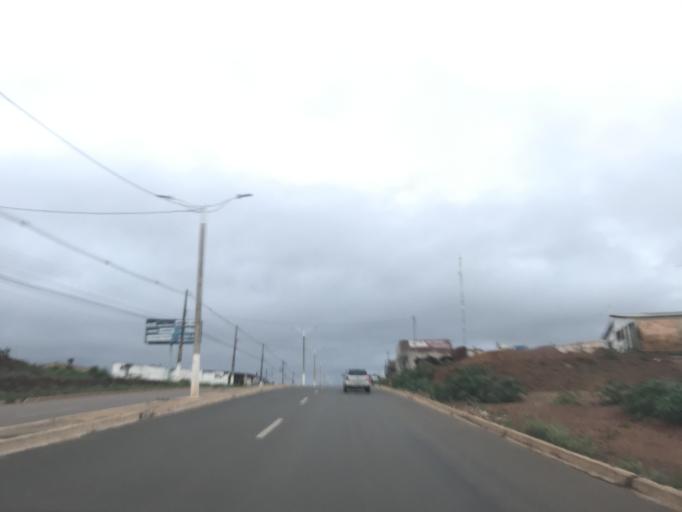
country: BR
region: Goias
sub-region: Luziania
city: Luziania
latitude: -16.2168
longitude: -47.9320
